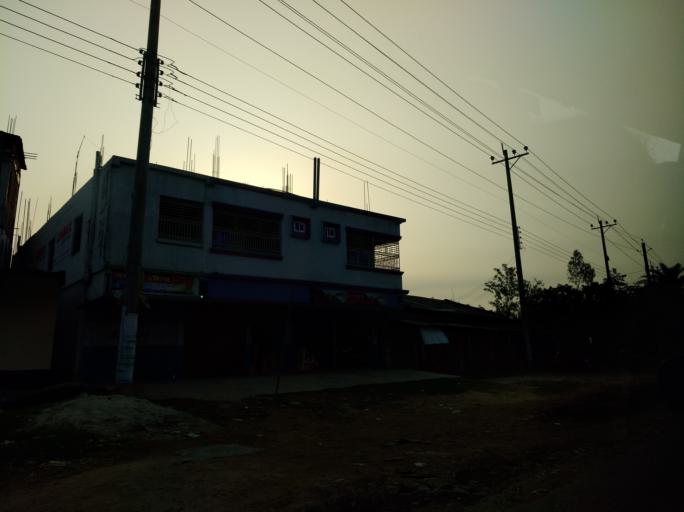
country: BD
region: Rajshahi
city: Bogra
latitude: 24.7001
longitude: 89.4011
